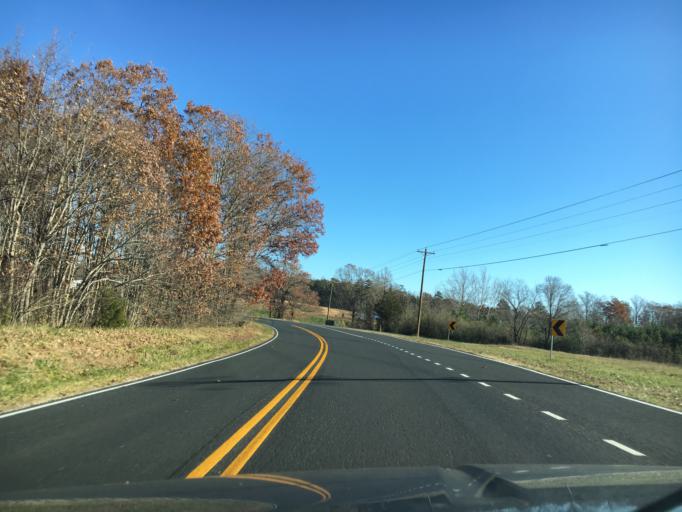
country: US
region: Virginia
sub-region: Appomattox County
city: Appomattox
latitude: 37.4274
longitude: -78.7279
